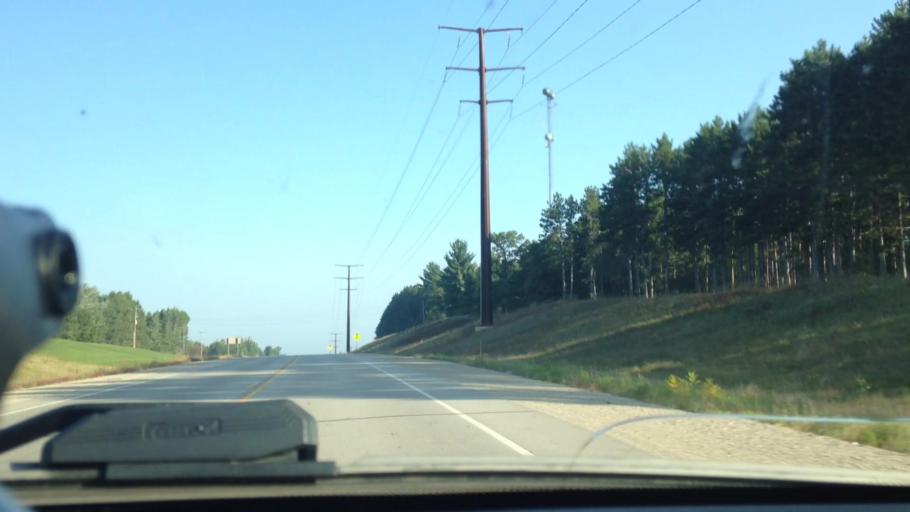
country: US
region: Wisconsin
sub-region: Marinette County
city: Peshtigo
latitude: 45.2115
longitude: -87.9950
